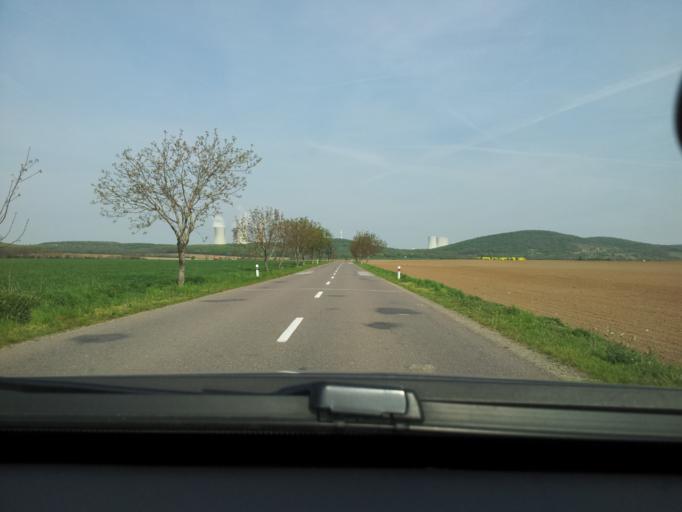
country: SK
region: Nitriansky
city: Tlmace
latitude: 48.2314
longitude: 18.4887
